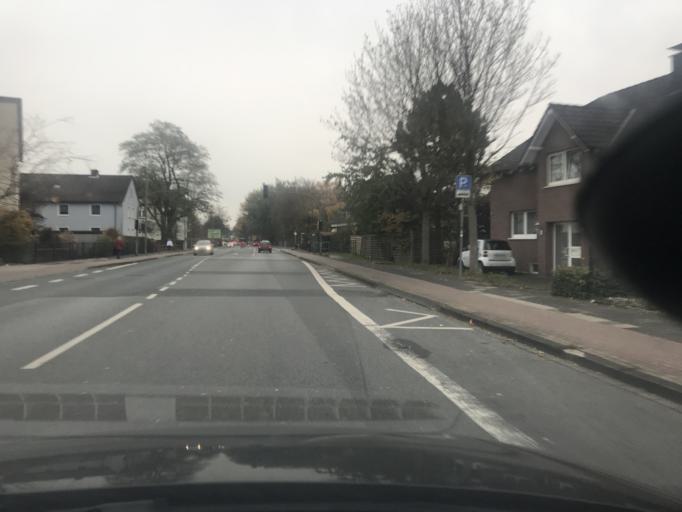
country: DE
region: North Rhine-Westphalia
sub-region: Regierungsbezirk Arnsberg
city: Hamm
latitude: 51.6903
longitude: 7.8782
